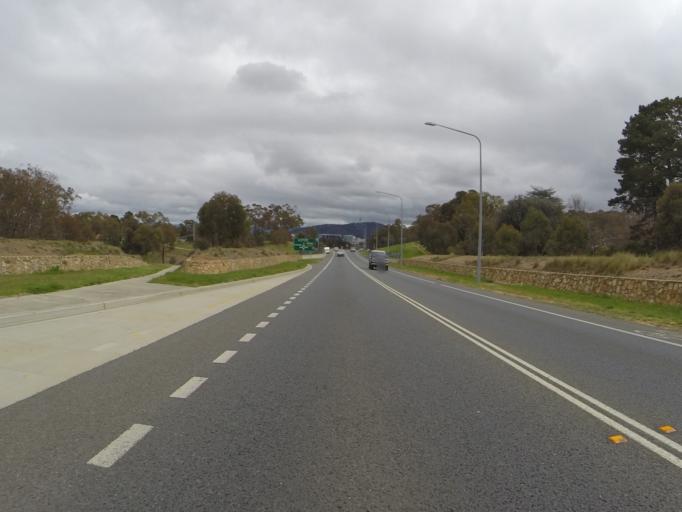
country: AU
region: Australian Capital Territory
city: Canberra
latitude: -35.2831
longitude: 149.1544
